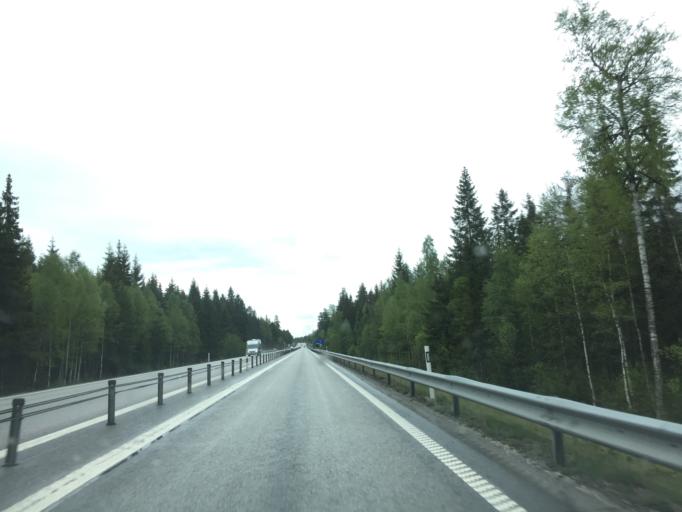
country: SE
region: OErebro
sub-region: Lindesbergs Kommun
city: Lindesberg
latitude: 59.5224
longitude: 15.1877
